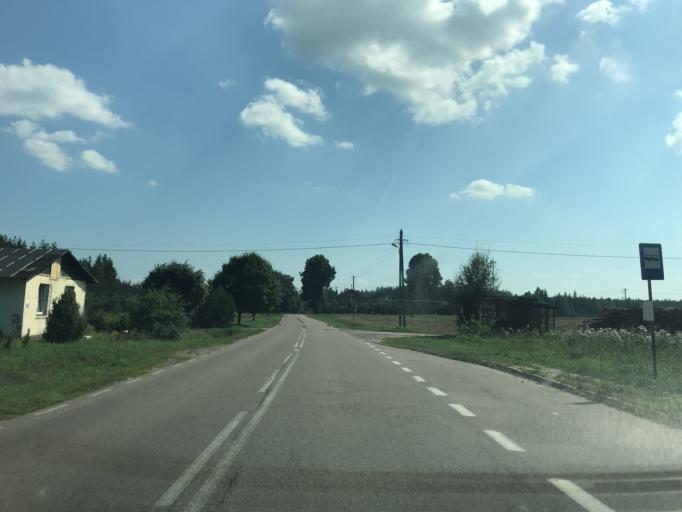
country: PL
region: Warmian-Masurian Voivodeship
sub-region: Powiat dzialdowski
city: Lidzbark
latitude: 53.1957
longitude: 19.8459
